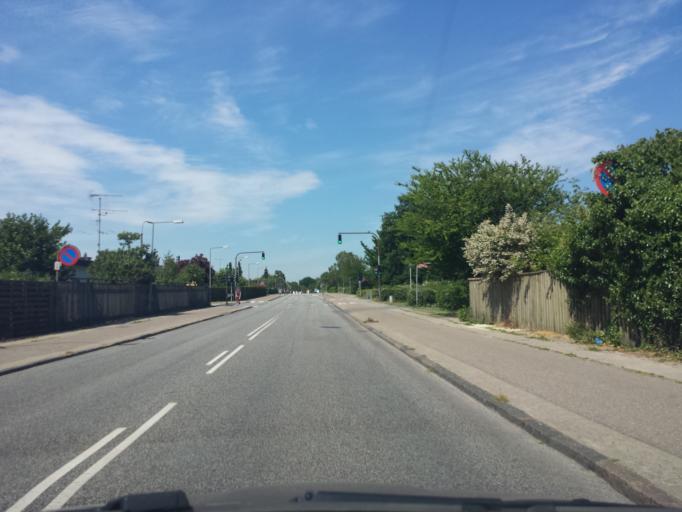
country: DK
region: Capital Region
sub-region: Ballerup Kommune
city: Ballerup
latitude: 55.7136
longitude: 12.3999
